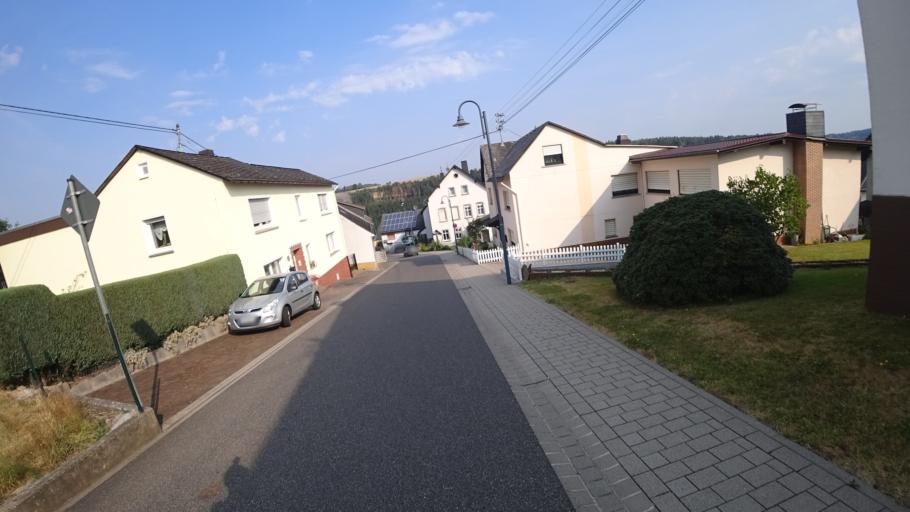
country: DE
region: Rheinland-Pfalz
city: Kammerforst
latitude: 50.4617
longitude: 7.6775
